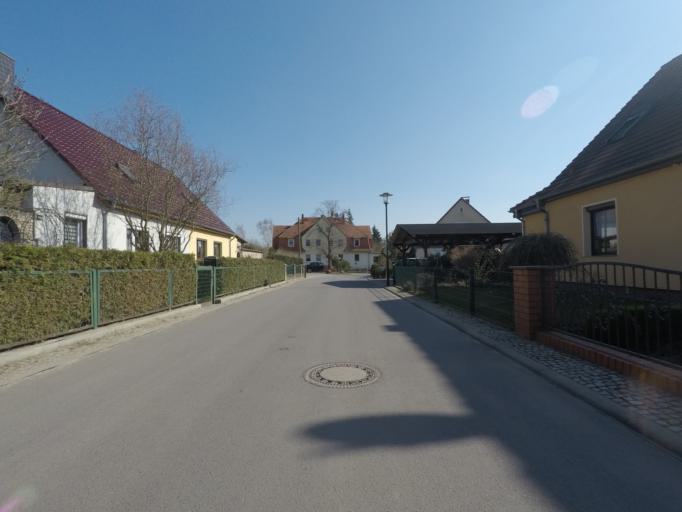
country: DE
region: Brandenburg
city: Eberswalde
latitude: 52.8406
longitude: 13.7961
